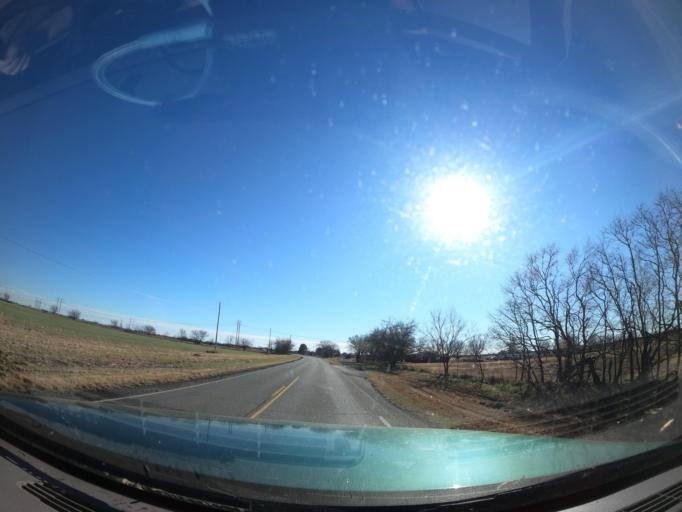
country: US
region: Oklahoma
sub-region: McIntosh County
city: Checotah
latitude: 35.5785
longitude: -95.6599
